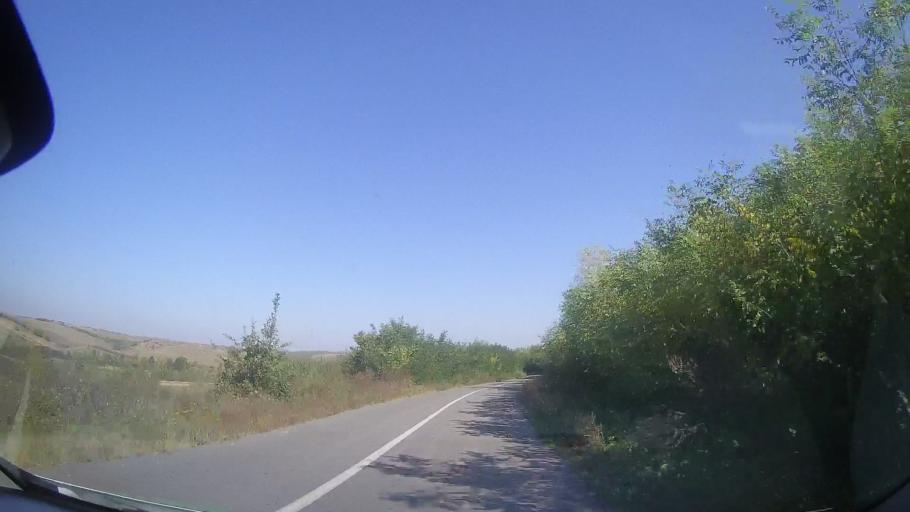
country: RO
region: Timis
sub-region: Comuna Balint
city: Balint
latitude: 45.8339
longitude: 21.8555
